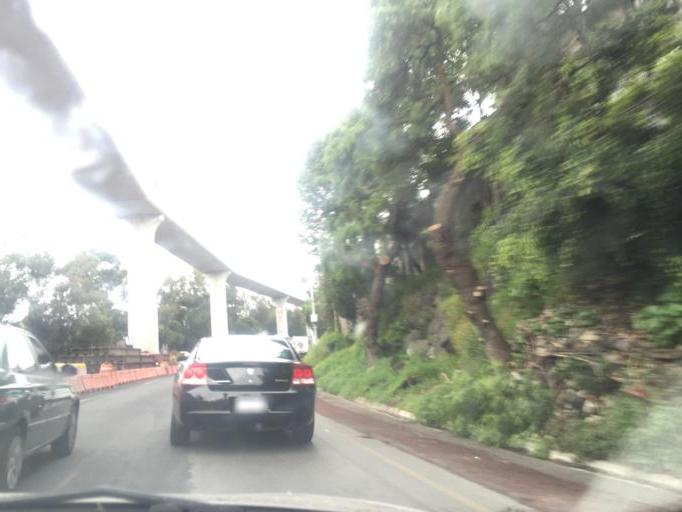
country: MX
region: Mexico City
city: Tlalpan
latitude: 19.2528
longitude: -99.1560
